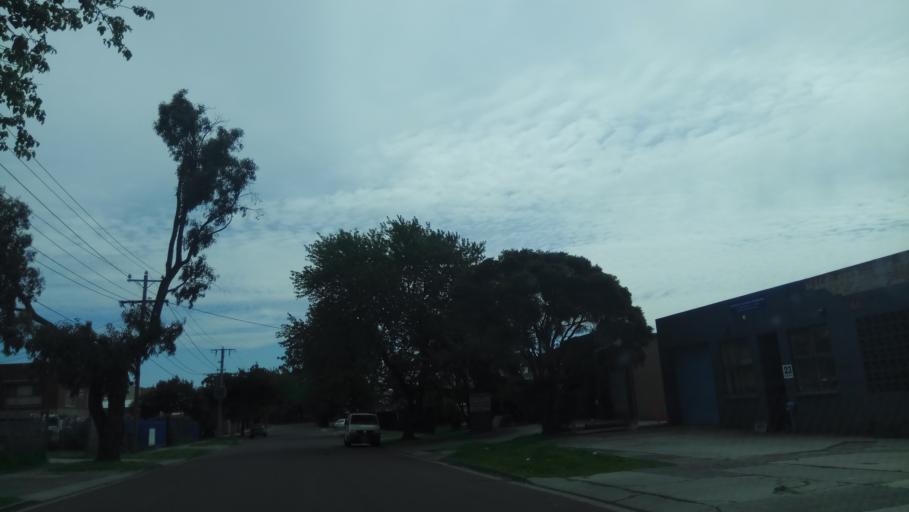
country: AU
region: Victoria
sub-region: Greater Dandenong
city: Springvale
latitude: -37.9510
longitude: 145.1358
